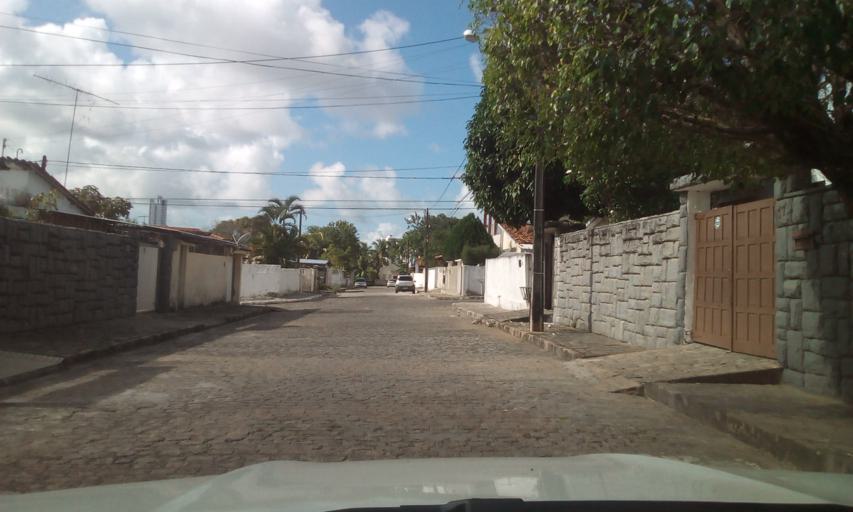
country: BR
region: Paraiba
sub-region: Joao Pessoa
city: Joao Pessoa
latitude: -7.1331
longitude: -34.8524
